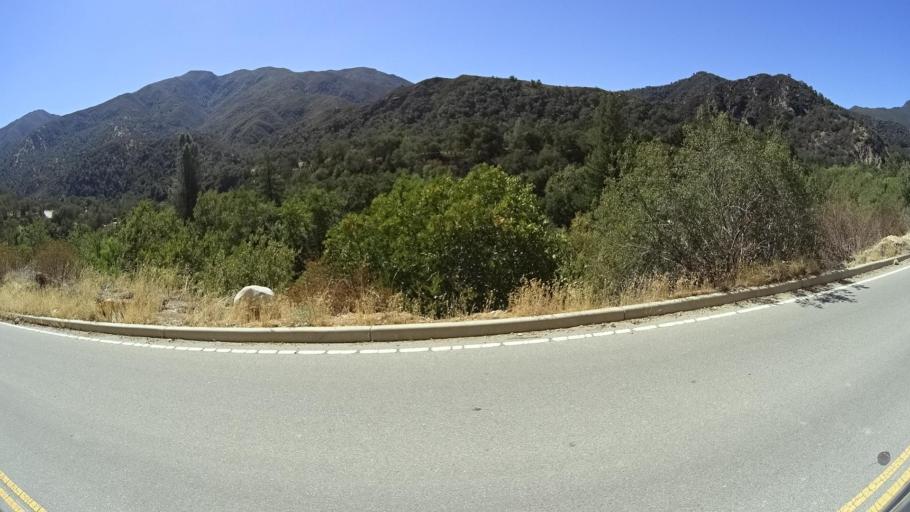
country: US
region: California
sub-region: Monterey County
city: Soledad
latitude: 36.2360
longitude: -121.4690
